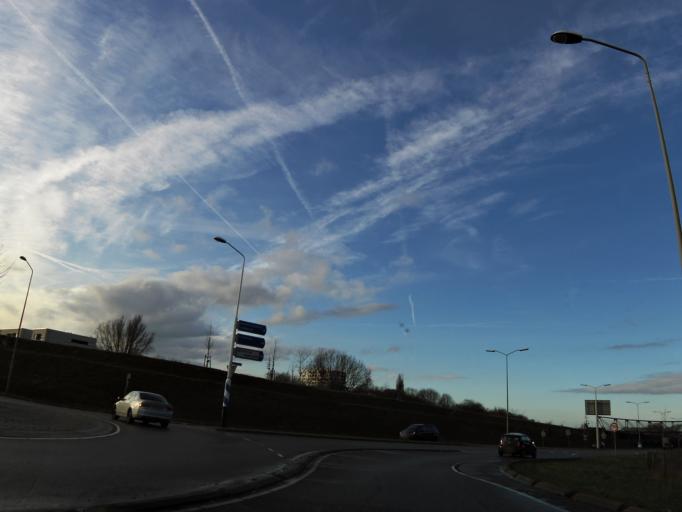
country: NL
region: Limburg
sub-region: Gemeente Heerlen
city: Heerlen
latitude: 50.8870
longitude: 6.0065
